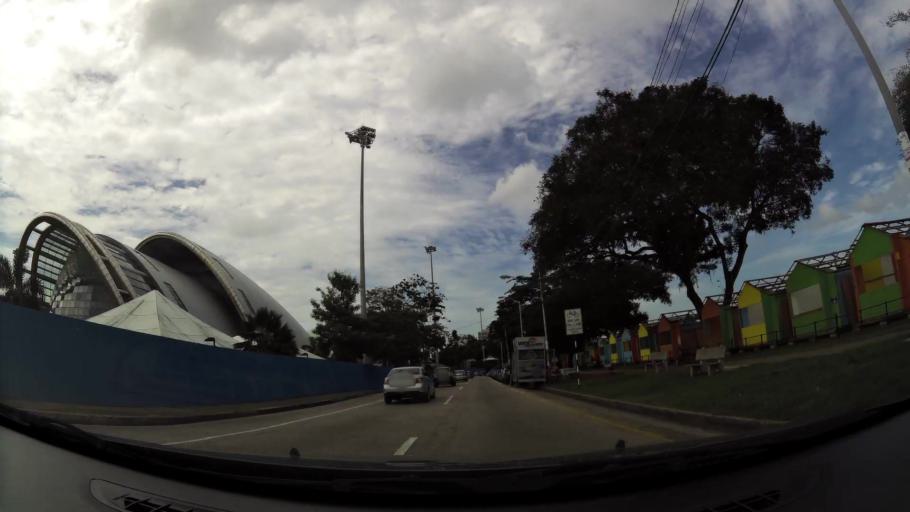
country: TT
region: City of Port of Spain
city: Port-of-Spain
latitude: 10.6644
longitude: -61.5102
